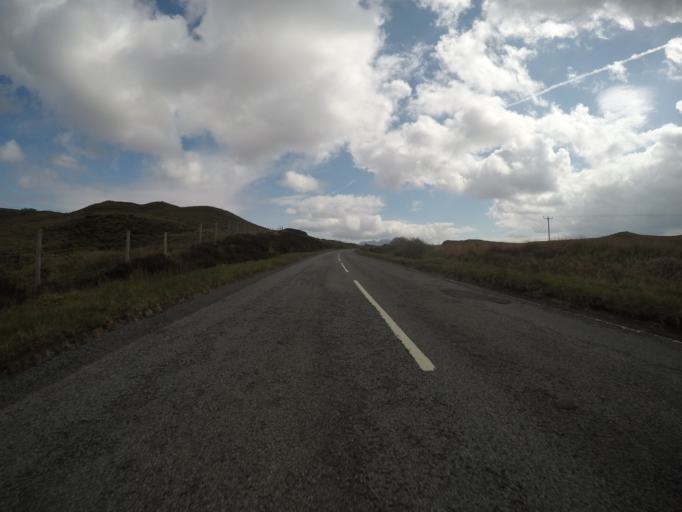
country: GB
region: Scotland
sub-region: Highland
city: Isle of Skye
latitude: 57.3198
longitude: -6.3241
